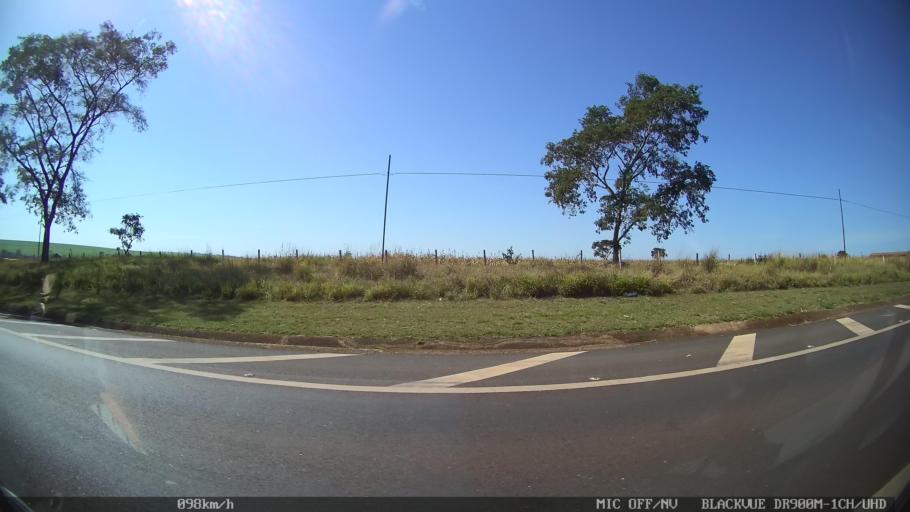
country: BR
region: Sao Paulo
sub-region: Batatais
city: Batatais
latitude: -20.8571
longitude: -47.6007
